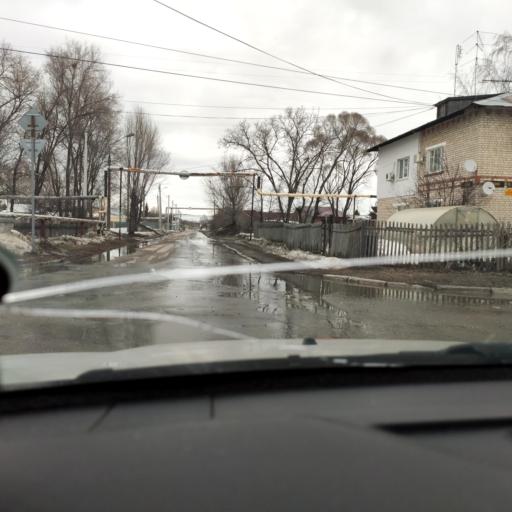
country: RU
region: Samara
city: Kurumoch
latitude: 53.4880
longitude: 50.0350
